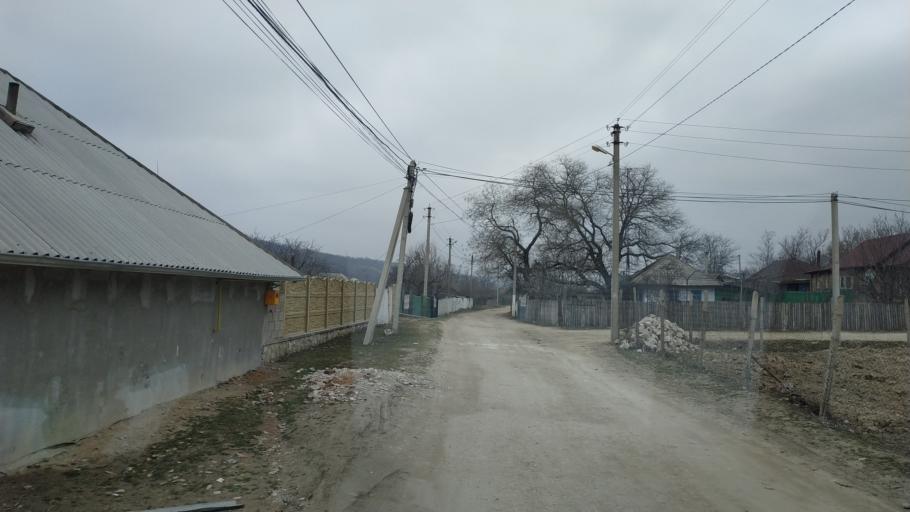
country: MD
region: Hincesti
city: Hincesti
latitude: 46.8861
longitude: 28.4055
